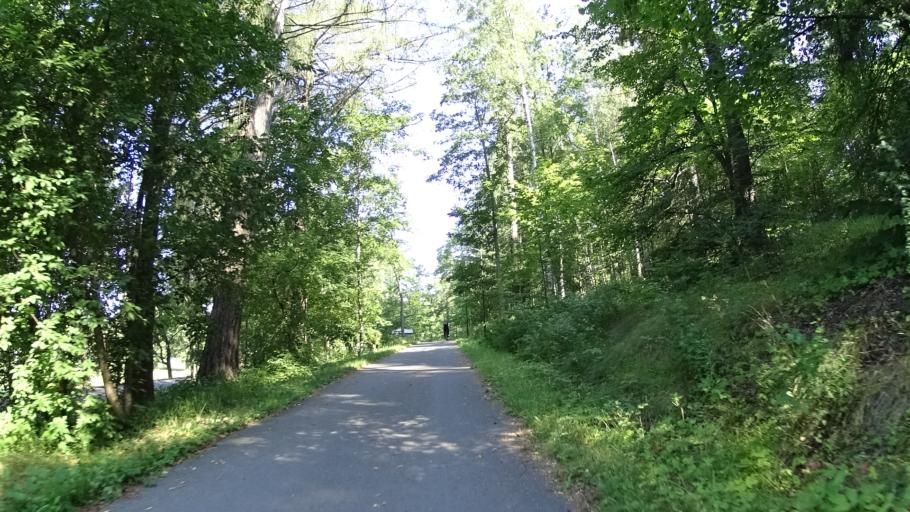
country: FI
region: Haeme
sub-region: Haemeenlinna
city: Haemeenlinna
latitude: 61.0250
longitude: 24.4456
